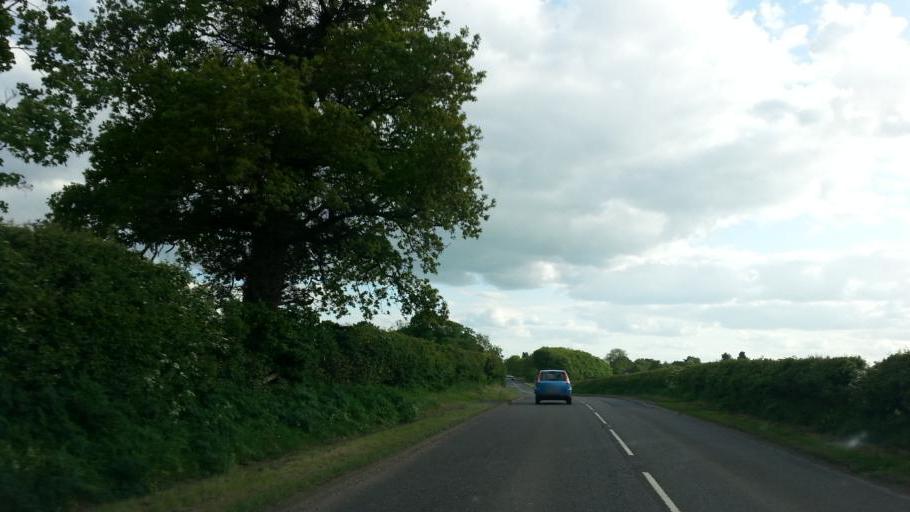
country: GB
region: England
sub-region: Nottinghamshire
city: South Collingham
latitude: 53.1097
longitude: -0.7765
